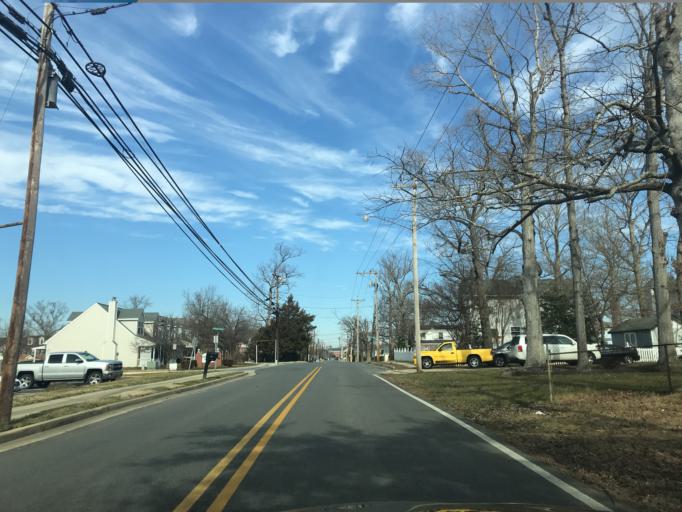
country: US
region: Maryland
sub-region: Charles County
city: La Plata
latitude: 38.5234
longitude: -76.9782
